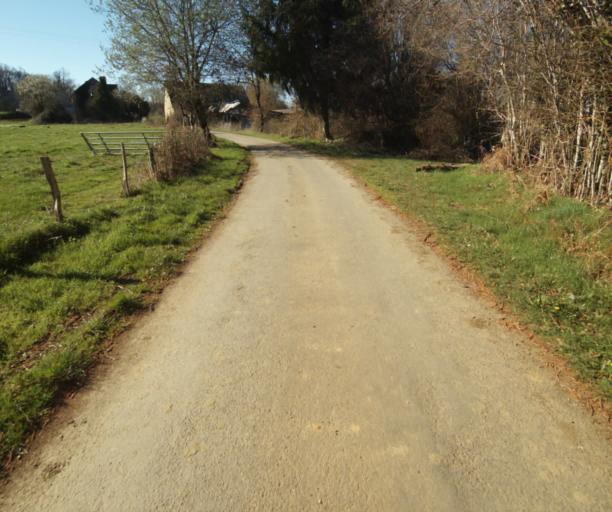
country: FR
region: Limousin
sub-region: Departement de la Correze
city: Chamboulive
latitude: 45.4006
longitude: 1.7085
